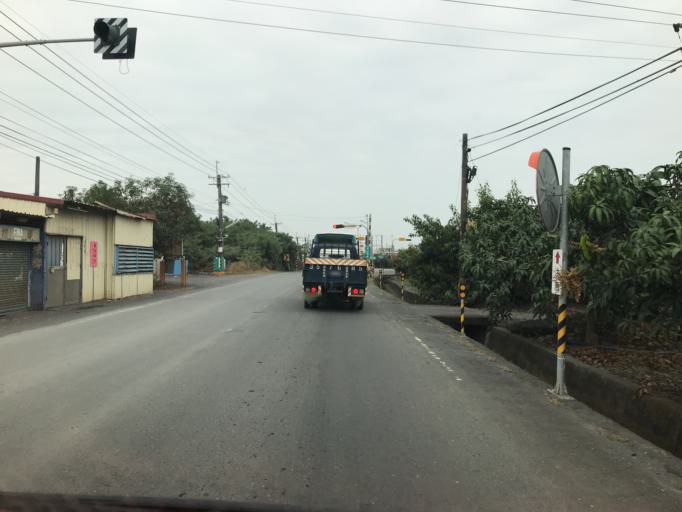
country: TW
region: Taiwan
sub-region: Pingtung
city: Pingtung
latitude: 22.5026
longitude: 120.5884
